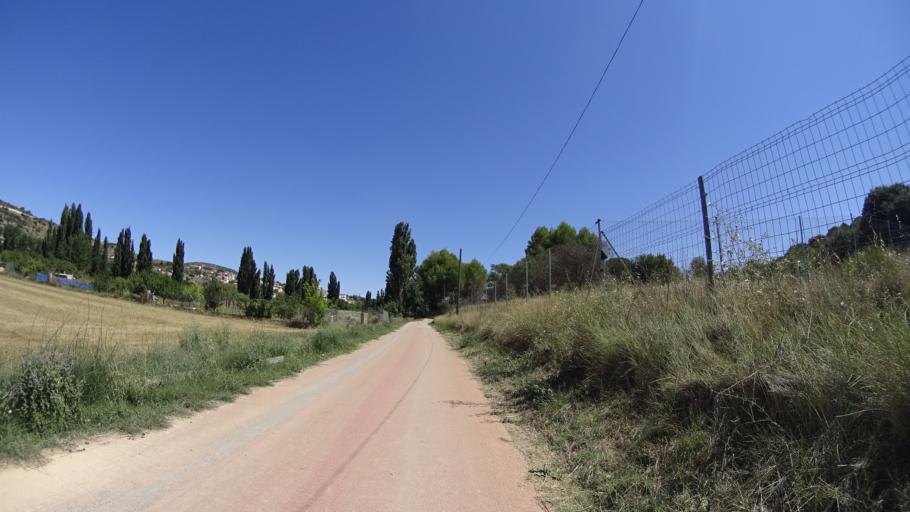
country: ES
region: Madrid
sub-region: Provincia de Madrid
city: Carabana
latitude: 40.2752
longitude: -3.2137
